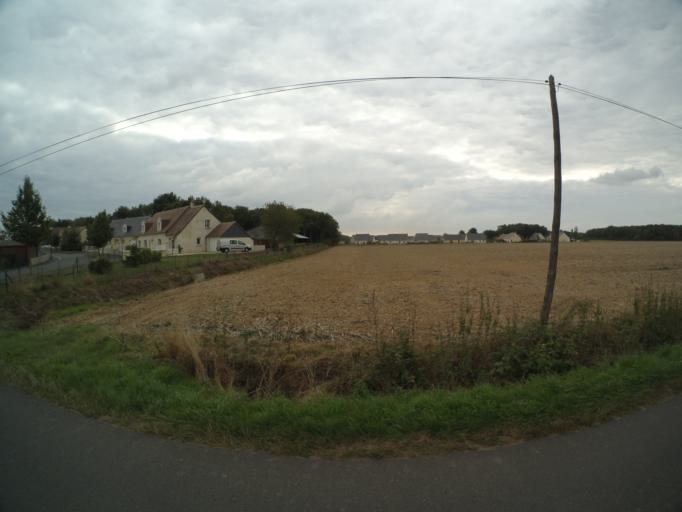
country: FR
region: Centre
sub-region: Departement d'Indre-et-Loire
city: Nazelles-Negron
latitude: 47.4888
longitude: 0.9442
